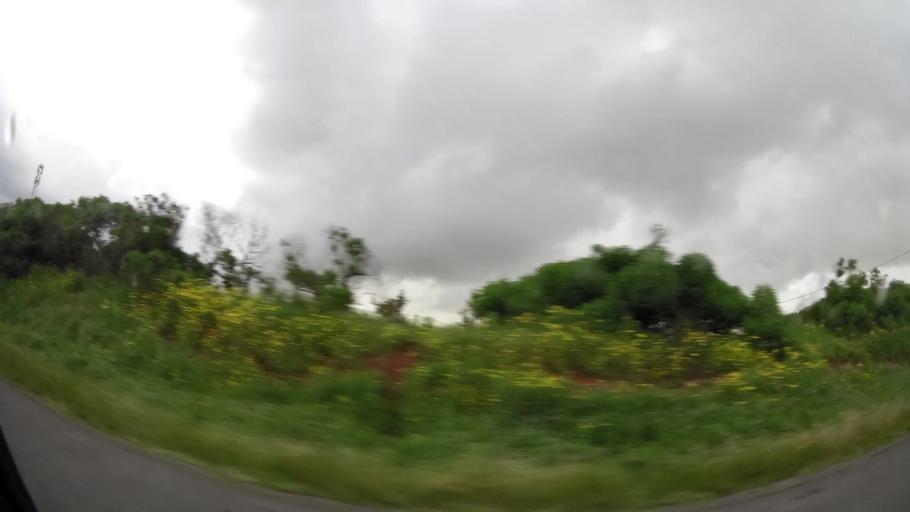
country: MA
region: Grand Casablanca
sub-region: Mohammedia
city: Mohammedia
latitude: 33.6214
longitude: -7.4315
